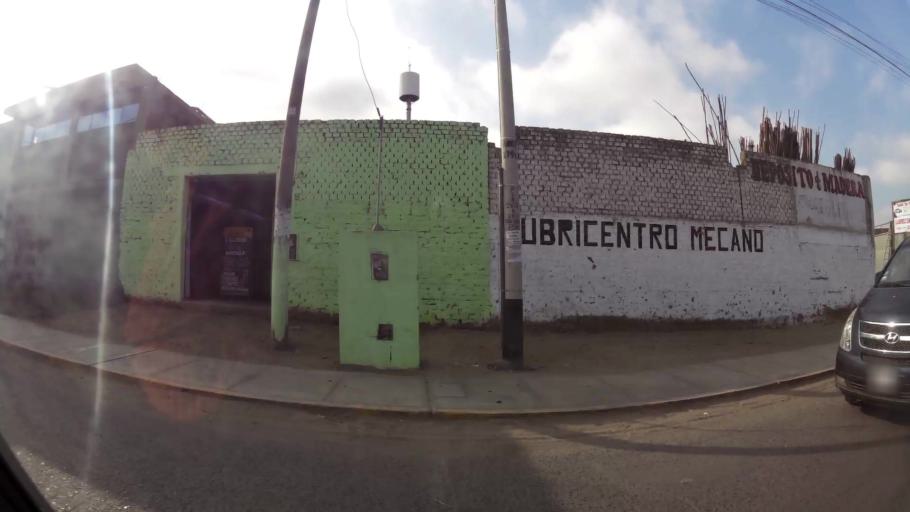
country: PE
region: La Libertad
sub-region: Provincia de Trujillo
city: Trujillo
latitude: -8.0927
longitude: -79.0237
